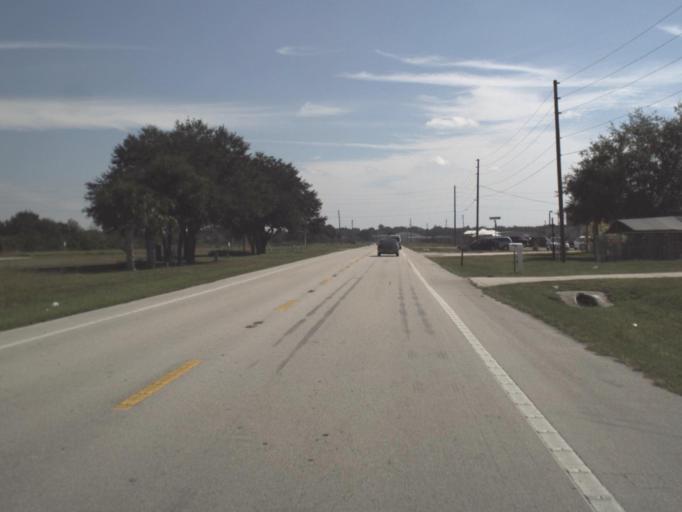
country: US
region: Florida
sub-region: Highlands County
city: Avon Park
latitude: 27.5962
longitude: -81.5326
